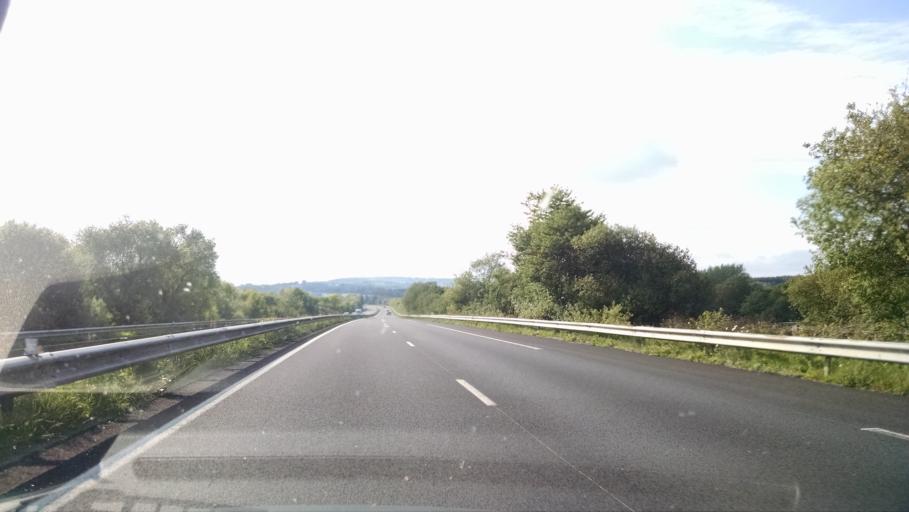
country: FR
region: Brittany
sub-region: Departement des Cotes-d'Armor
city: Plounevez-Moedec
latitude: 48.5520
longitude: -3.4689
